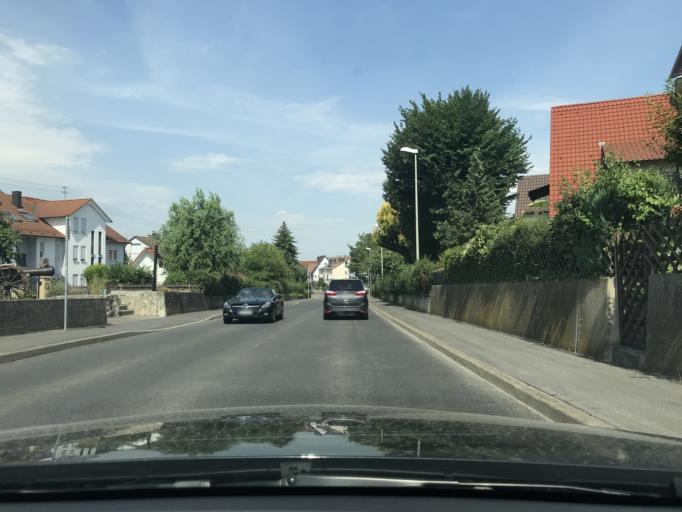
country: DE
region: Baden-Wuerttemberg
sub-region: Regierungsbezirk Stuttgart
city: Waiblingen
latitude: 48.8630
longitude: 9.3191
